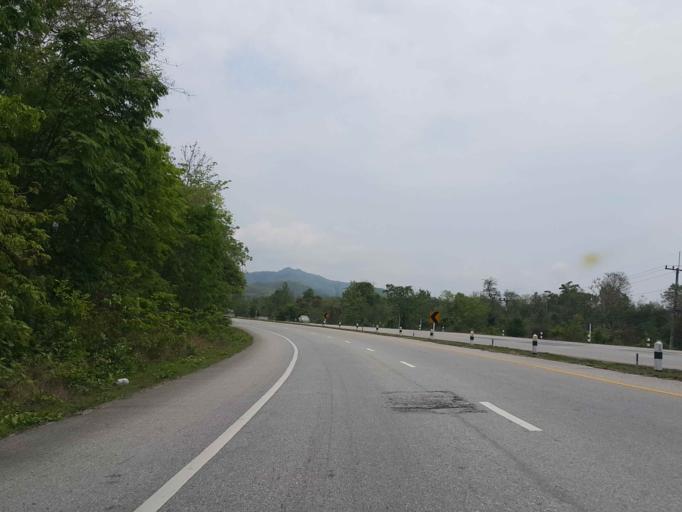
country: TH
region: Lampang
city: Thoen
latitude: 17.7433
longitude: 99.2308
